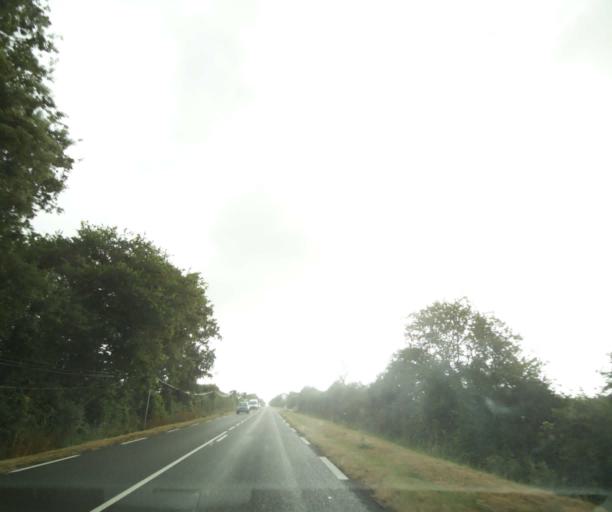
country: FR
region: Pays de la Loire
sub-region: Departement de la Vendee
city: Saint-Hilaire-de-Talmont
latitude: 46.4679
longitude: -1.5822
